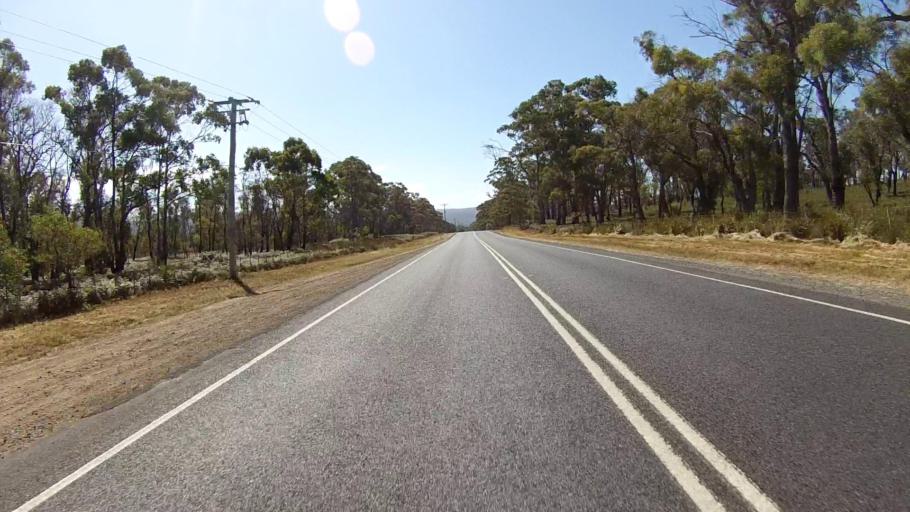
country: AU
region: Tasmania
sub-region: Sorell
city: Sorell
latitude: -42.5378
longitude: 147.8977
